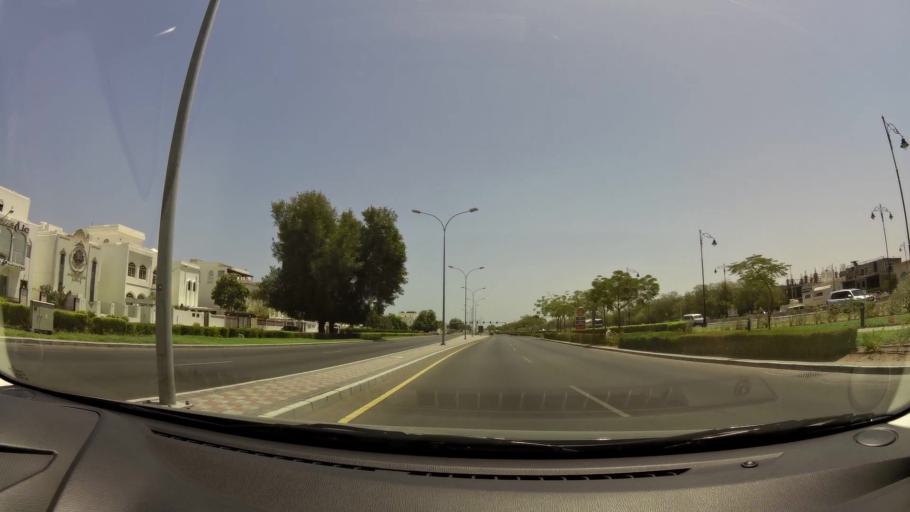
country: OM
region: Muhafazat Masqat
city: Bawshar
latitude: 23.6009
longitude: 58.4457
